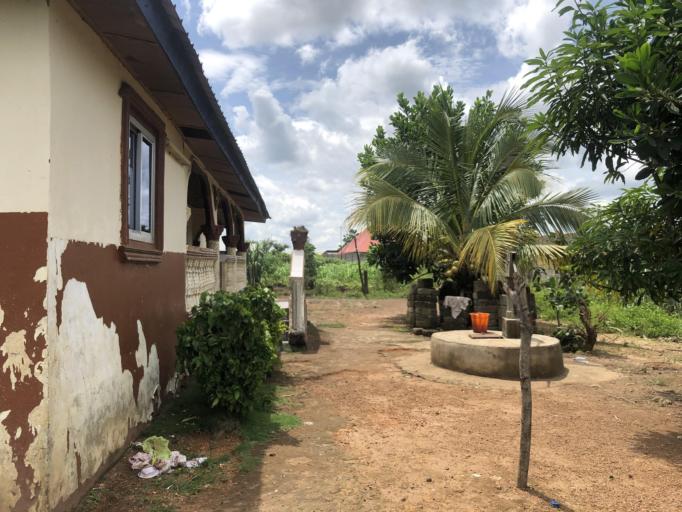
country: SL
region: Northern Province
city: Magburaka
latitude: 8.7008
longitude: -11.9249
